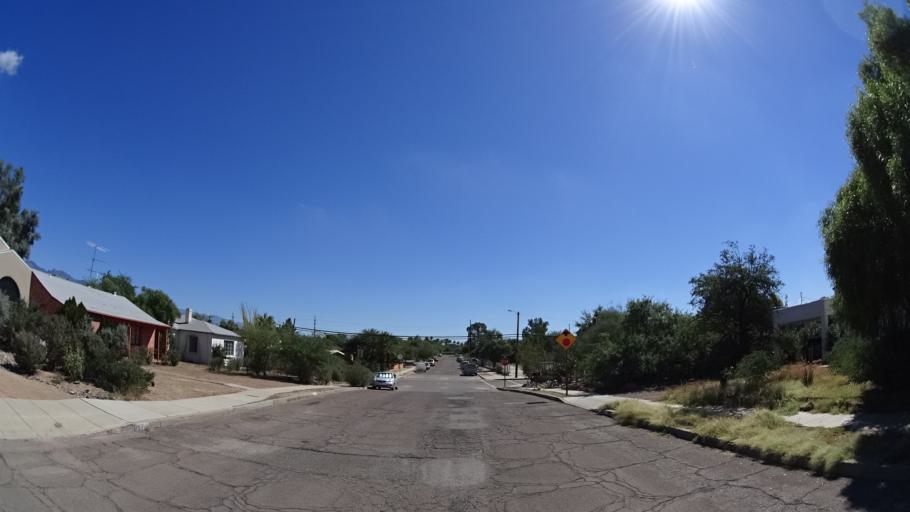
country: US
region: Arizona
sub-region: Pima County
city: Tucson
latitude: 32.2478
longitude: -110.9475
